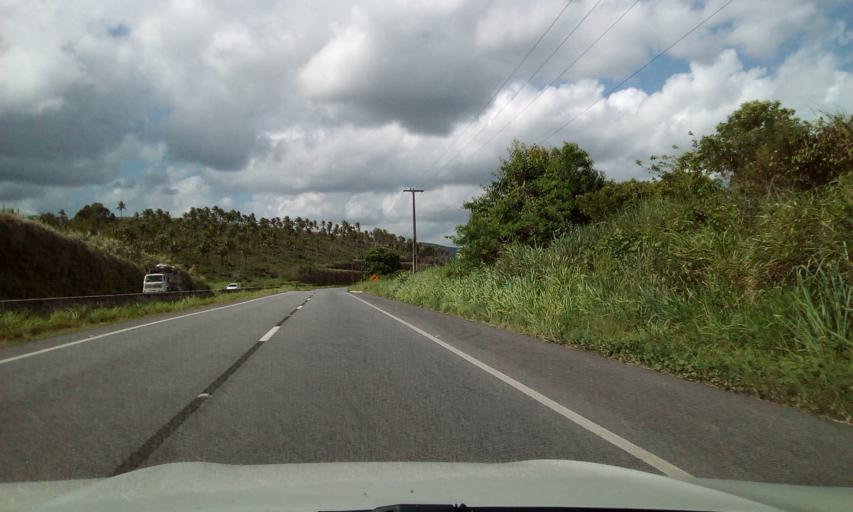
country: BR
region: Alagoas
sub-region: Messias
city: Messias
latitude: -9.3213
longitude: -35.8305
